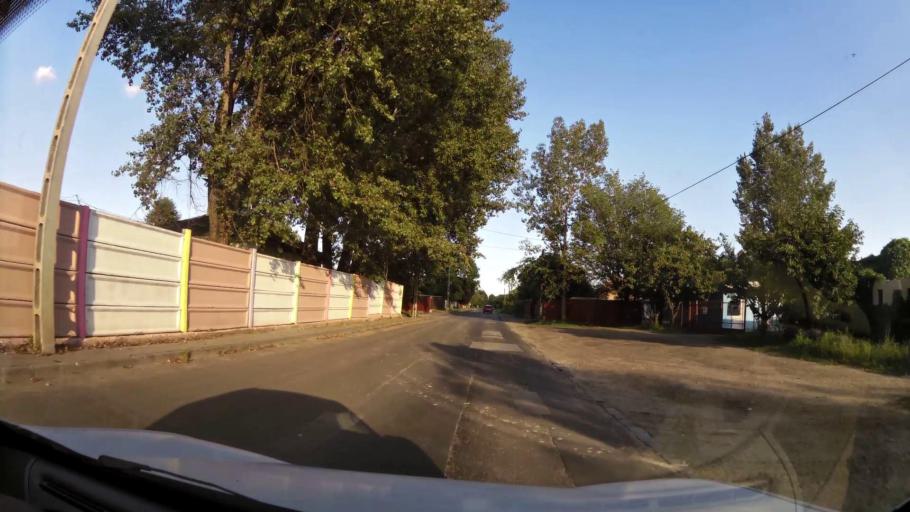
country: HU
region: Budapest
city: Budapest XVI. keruelet
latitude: 47.5017
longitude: 19.1745
